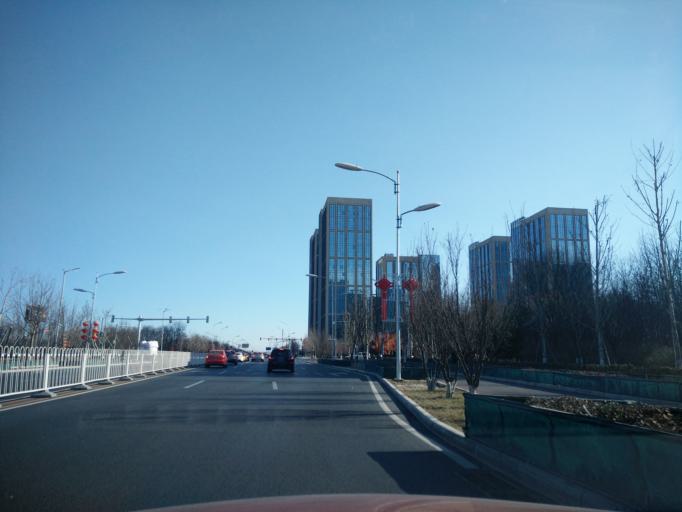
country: CN
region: Beijing
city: Jiugong
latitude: 39.8072
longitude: 116.4894
